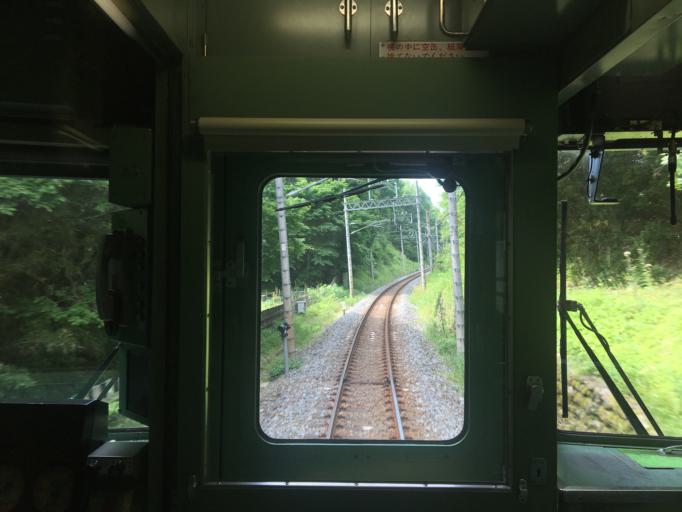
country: JP
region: Saitama
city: Ogawa
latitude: 36.0854
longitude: 139.2358
